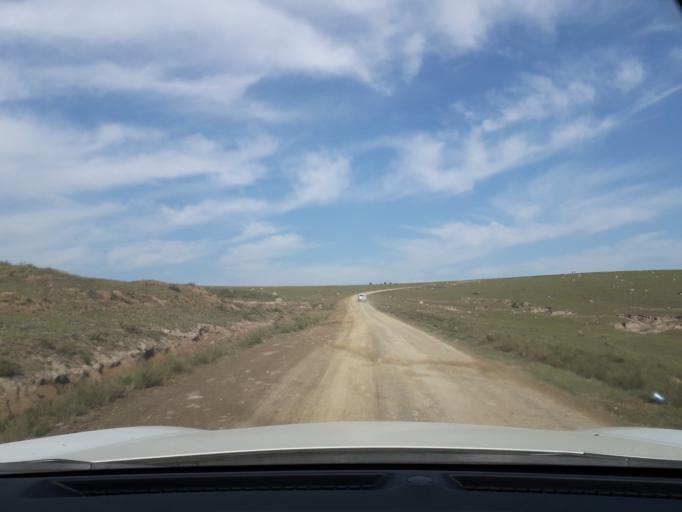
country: ZA
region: Eastern Cape
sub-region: Buffalo City Metropolitan Municipality
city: Bhisho
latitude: -33.0033
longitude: 27.3174
